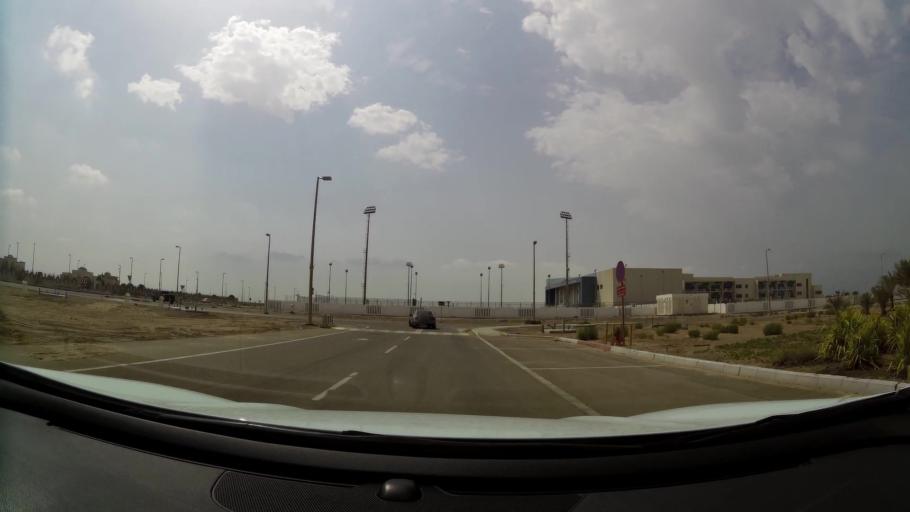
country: AE
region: Abu Dhabi
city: Abu Dhabi
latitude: 24.5382
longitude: 54.6333
